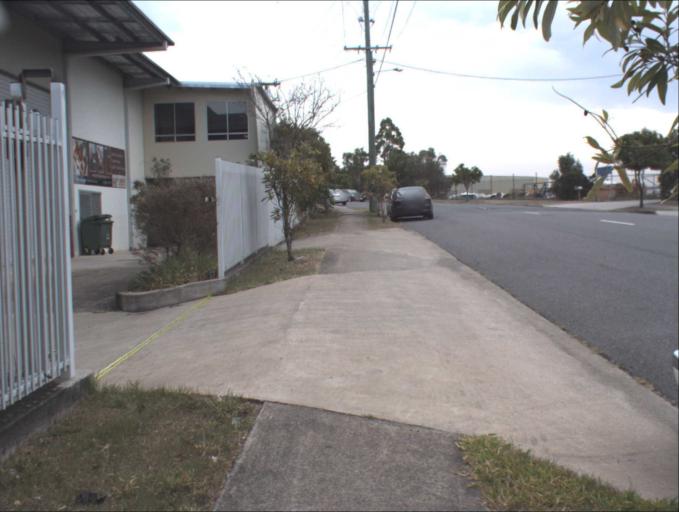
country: AU
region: Queensland
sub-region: Logan
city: Beenleigh
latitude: -27.6814
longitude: 153.1939
